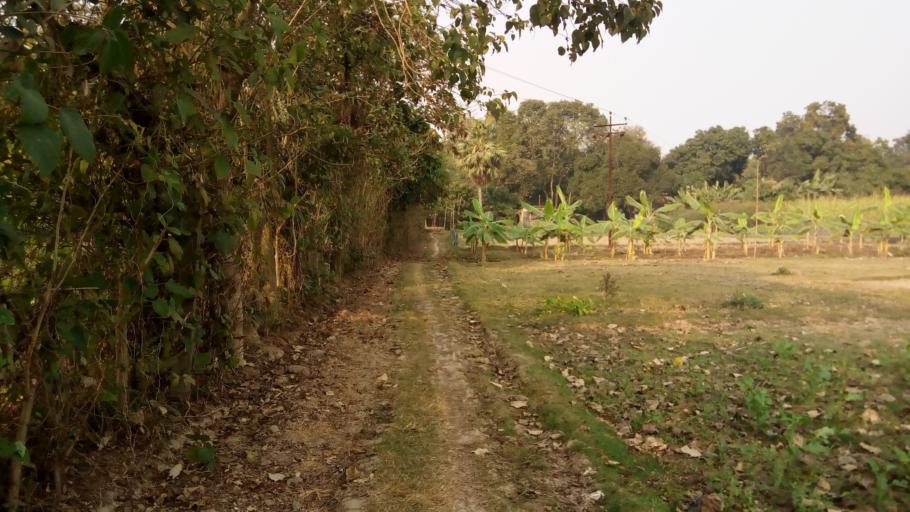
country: IN
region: West Bengal
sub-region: Nadia
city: Navadwip
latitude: 23.4464
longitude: 88.4178
